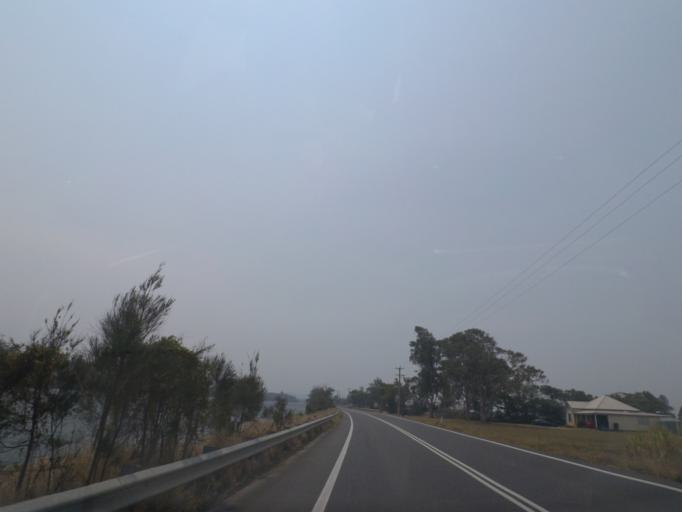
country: AU
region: New South Wales
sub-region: Richmond Valley
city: Evans Head
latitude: -28.9888
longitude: 153.4626
